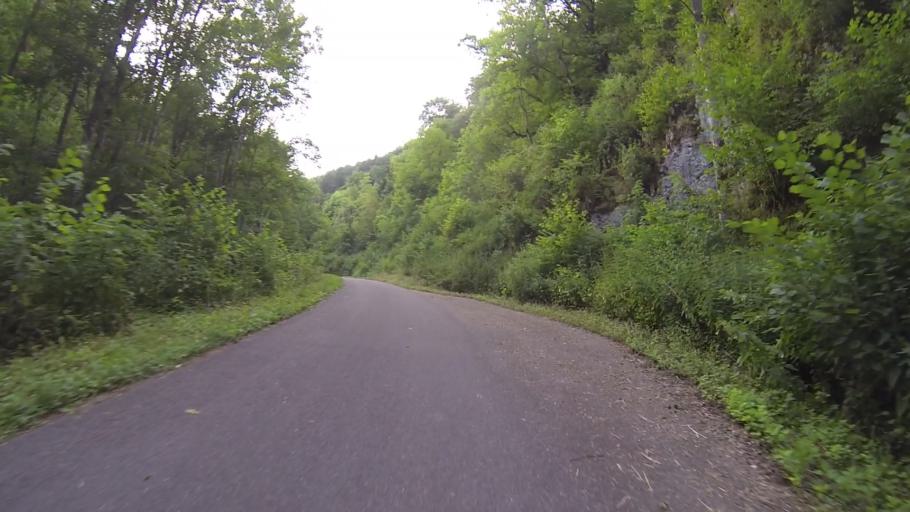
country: DE
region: Baden-Wuerttemberg
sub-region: Tuebingen Region
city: Blaubeuren
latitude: 48.4491
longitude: 9.8528
